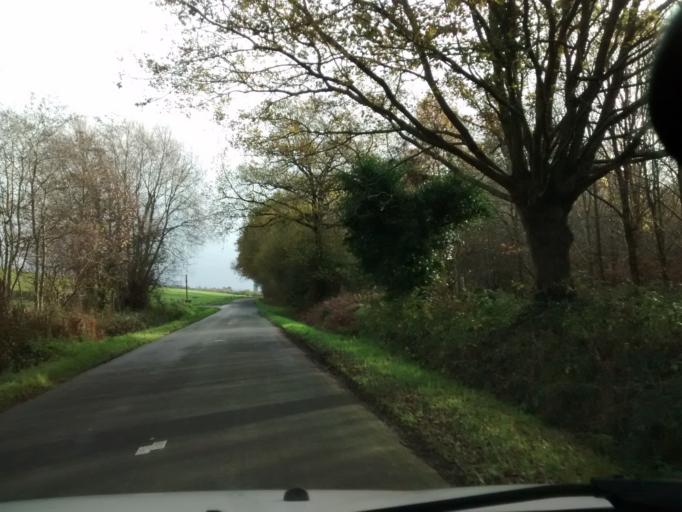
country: FR
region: Brittany
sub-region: Departement d'Ille-et-Vilaine
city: Montreuil-sous-Perouse
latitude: 48.1470
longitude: -1.2628
